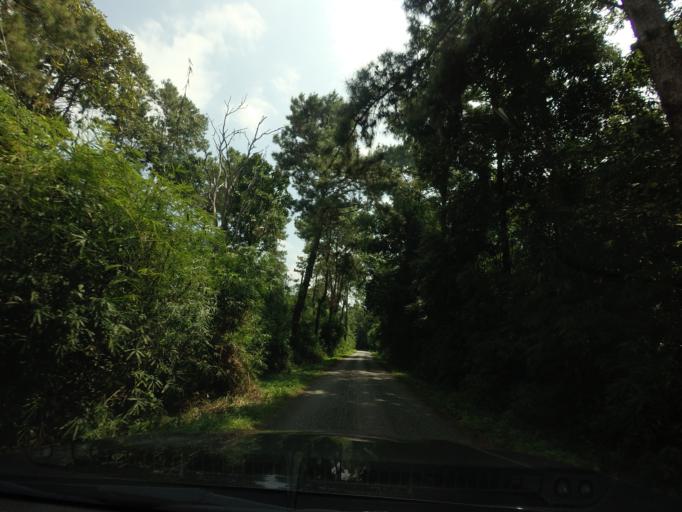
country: TH
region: Loei
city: Phu Ruea
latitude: 17.4720
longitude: 101.3541
